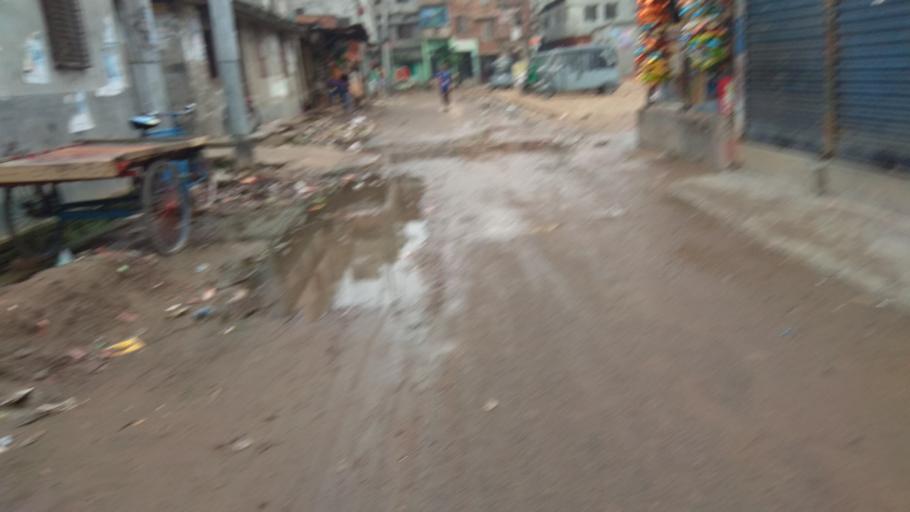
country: BD
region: Dhaka
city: Tungi
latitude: 23.8273
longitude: 90.3751
